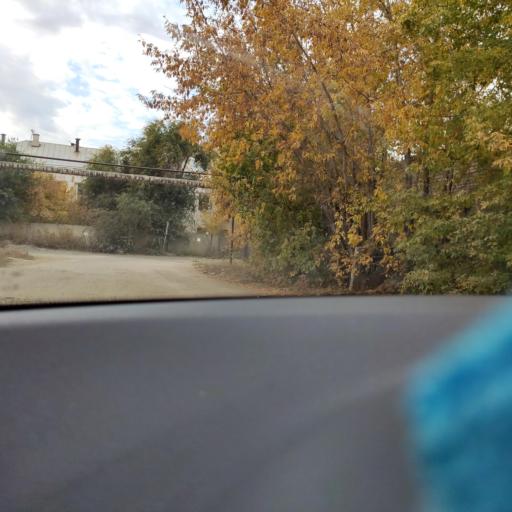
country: RU
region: Samara
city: Samara
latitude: 53.1938
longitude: 50.2634
